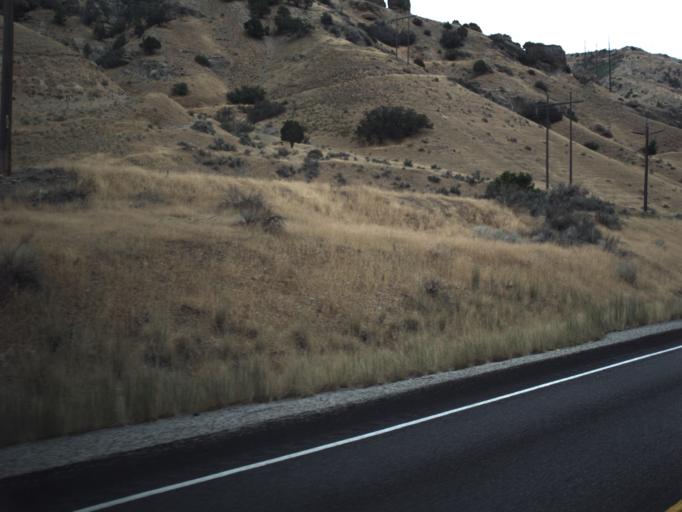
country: US
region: Utah
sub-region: Utah County
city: Mapleton
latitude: 39.9973
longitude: -111.4133
